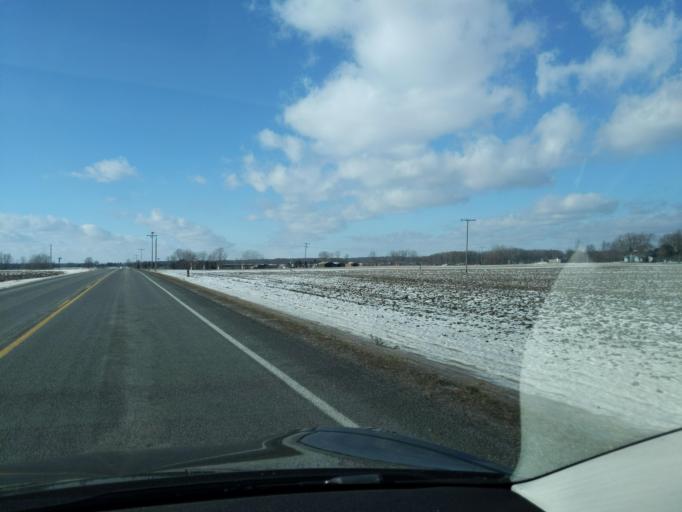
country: US
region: Michigan
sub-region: Ingham County
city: Williamston
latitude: 42.6010
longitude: -84.2969
